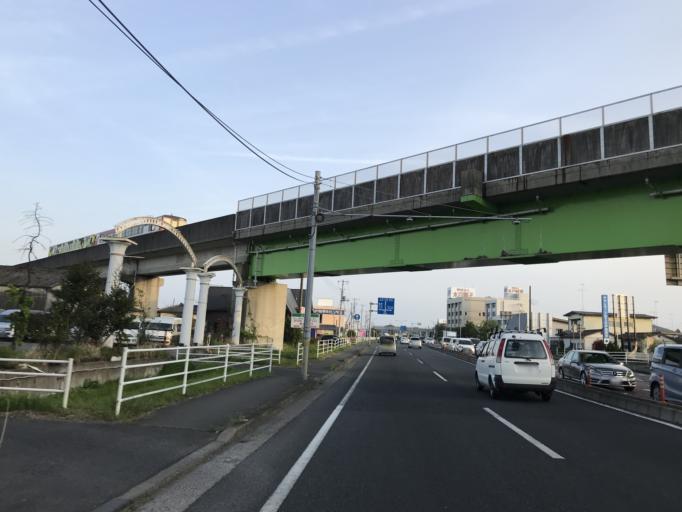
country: JP
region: Ibaraki
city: Katsuta
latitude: 36.3689
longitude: 140.5016
